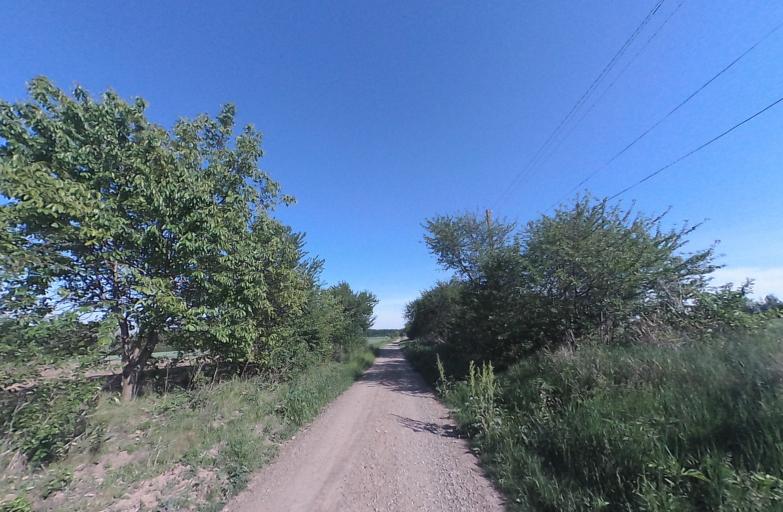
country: RO
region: Neamt
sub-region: Comuna Dulcesti
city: Dulcesti
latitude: 47.0024
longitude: 26.7750
